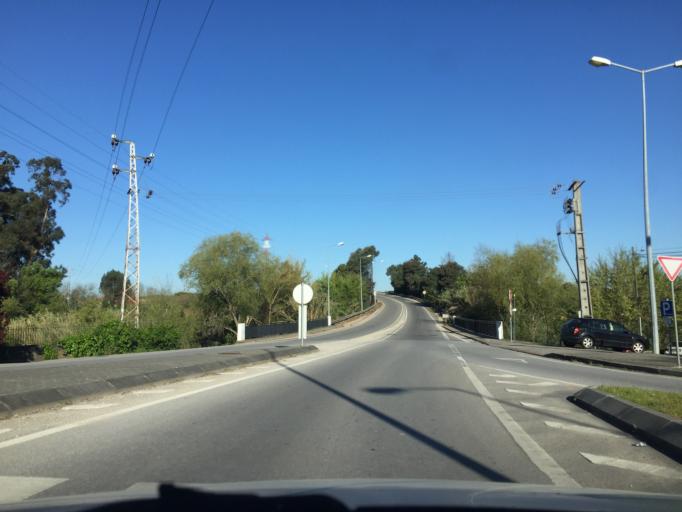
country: PT
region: Aveiro
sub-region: Anadia
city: Arcos
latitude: 40.4436
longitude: -8.4525
